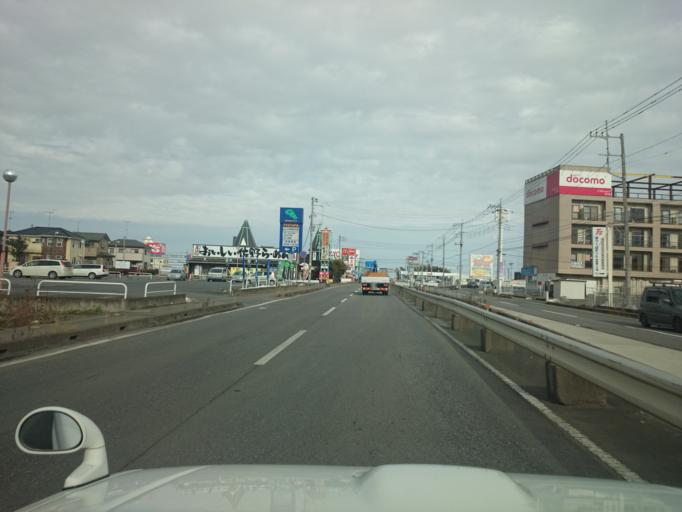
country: JP
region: Ibaraki
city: Ishige
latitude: 36.1070
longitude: 139.9842
